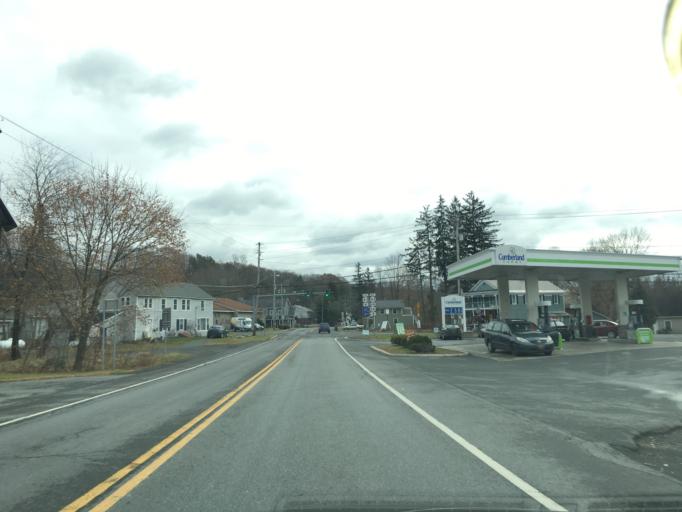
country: US
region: New York
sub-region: Rensselaer County
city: Averill Park
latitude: 42.6380
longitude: -73.5417
